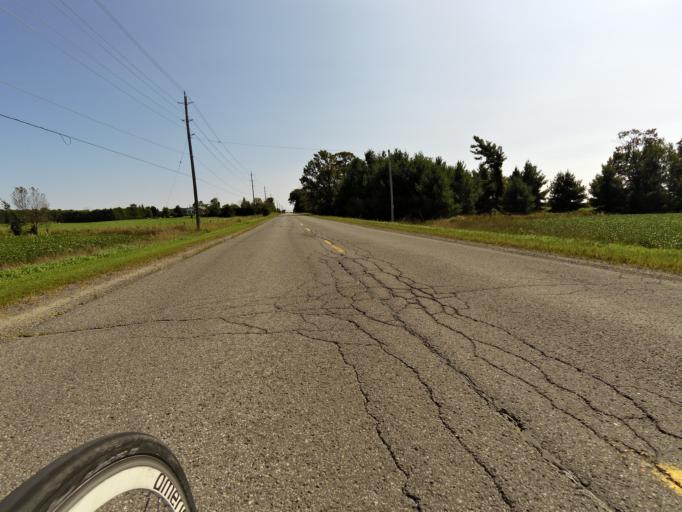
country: CA
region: Ontario
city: Arnprior
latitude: 45.4873
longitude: -76.1320
